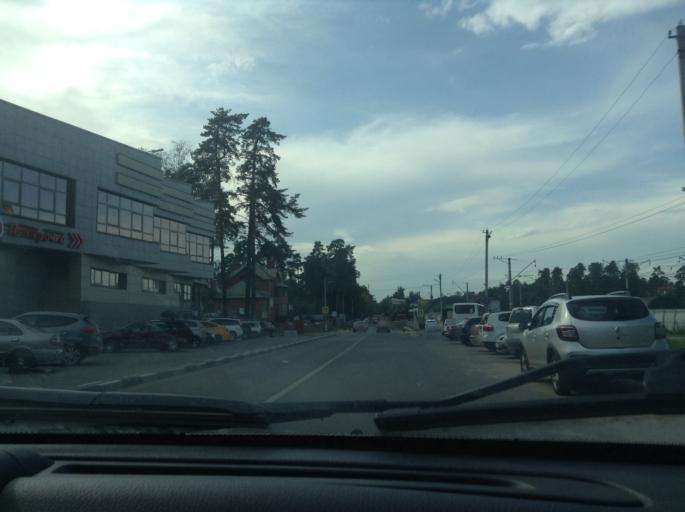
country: RU
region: Moskovskaya
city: Il'inskiy
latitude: 55.6146
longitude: 38.1039
